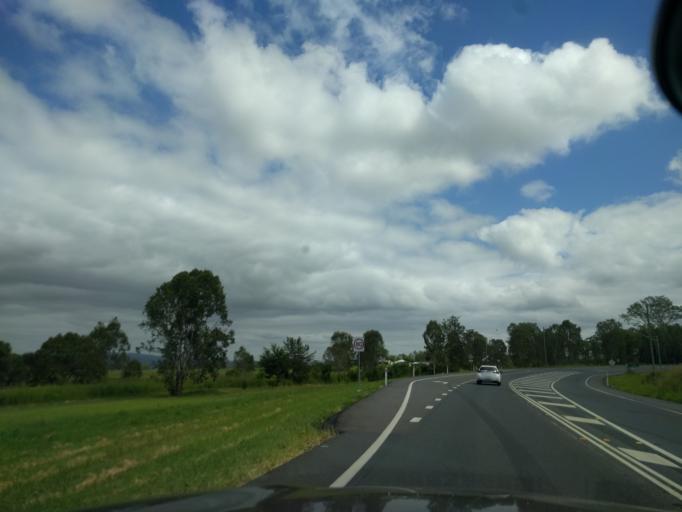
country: AU
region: Queensland
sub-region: Logan
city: Cedar Vale
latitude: -27.8924
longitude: 152.9735
